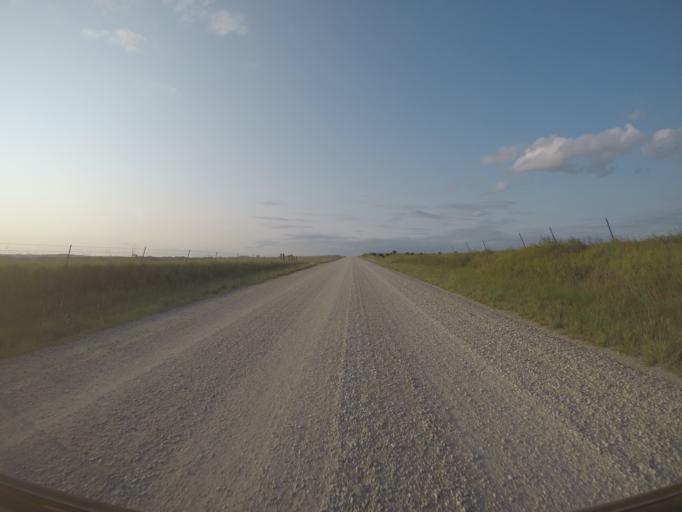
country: US
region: Kansas
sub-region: Pottawatomie County
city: Wamego
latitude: 39.1248
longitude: -96.4281
